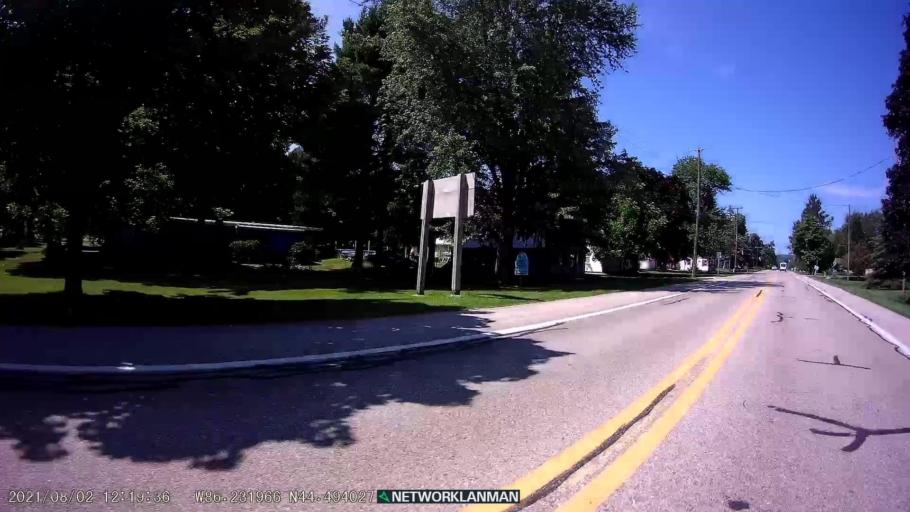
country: US
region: Michigan
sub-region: Benzie County
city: Frankfort
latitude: 44.4942
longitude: -86.2320
